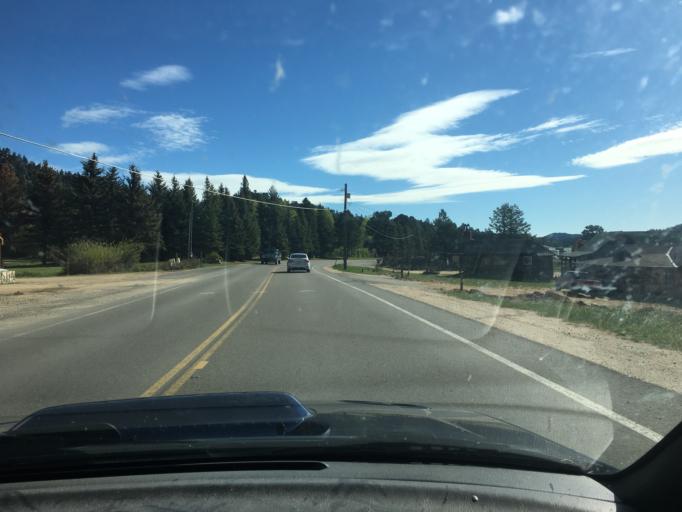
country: US
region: Colorado
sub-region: Larimer County
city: Estes Park
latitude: 40.3616
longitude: -105.5534
